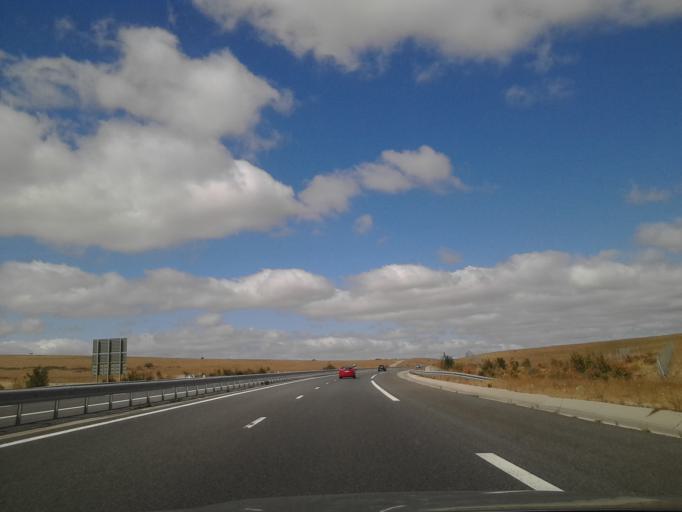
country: FR
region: Midi-Pyrenees
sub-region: Departement de l'Aveyron
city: Creissels
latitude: 44.0268
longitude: 3.0841
